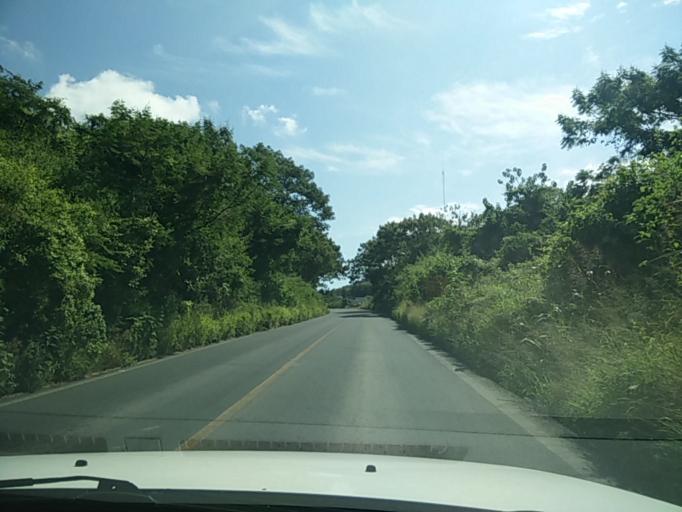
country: MX
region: Jalisco
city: Ajijic
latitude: 20.3027
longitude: -103.2292
